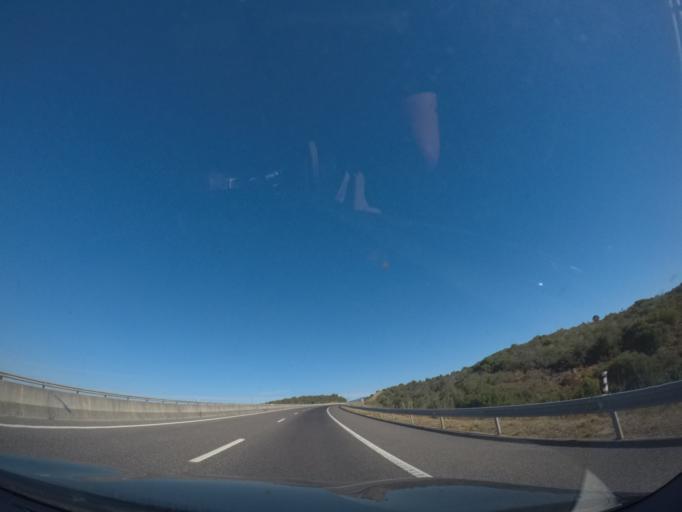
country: PT
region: Faro
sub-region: Lagoa
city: Estombar
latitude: 37.1649
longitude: -8.5112
